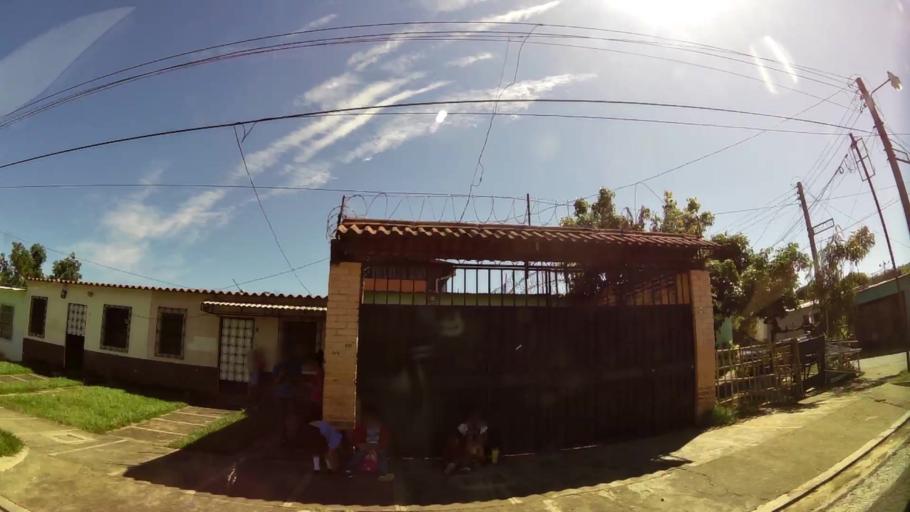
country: SV
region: Ahuachapan
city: Ahuachapan
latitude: 13.9184
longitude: -89.8546
